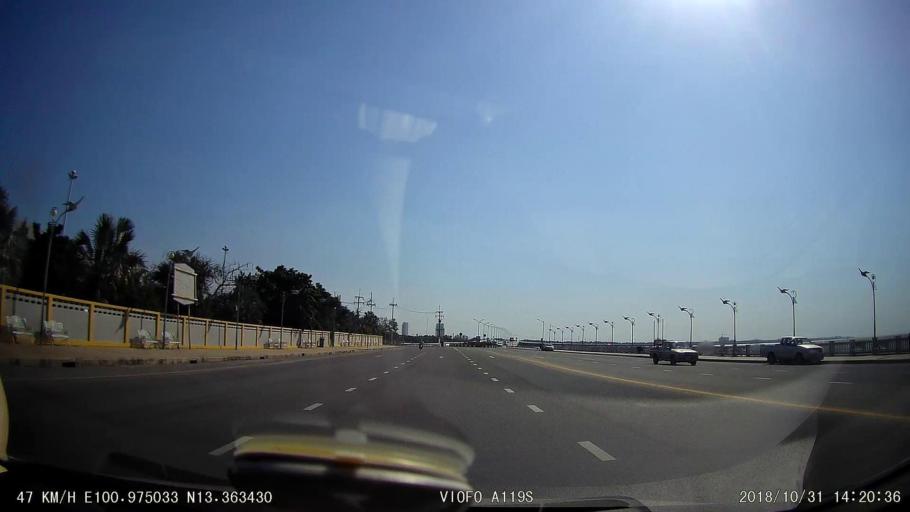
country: TH
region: Chon Buri
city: Chon Buri
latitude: 13.3633
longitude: 100.9751
